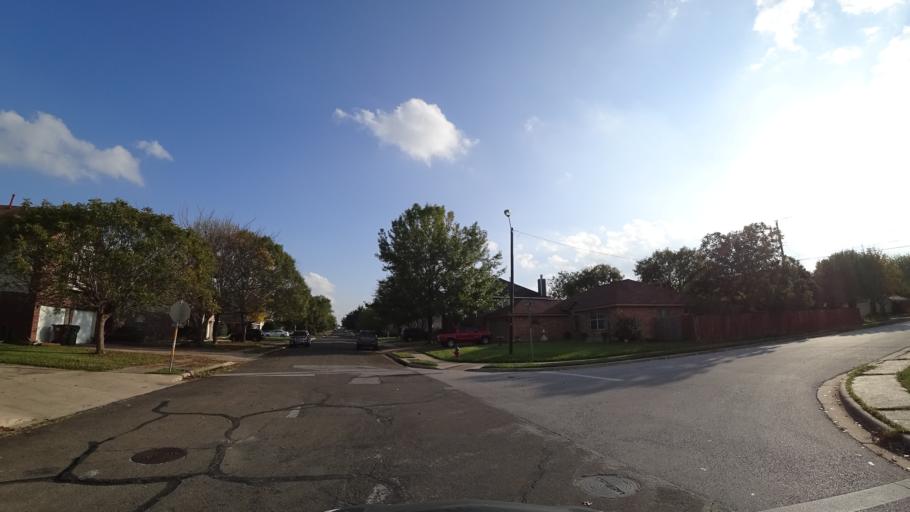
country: US
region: Texas
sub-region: Williamson County
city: Round Rock
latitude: 30.4954
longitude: -97.6633
